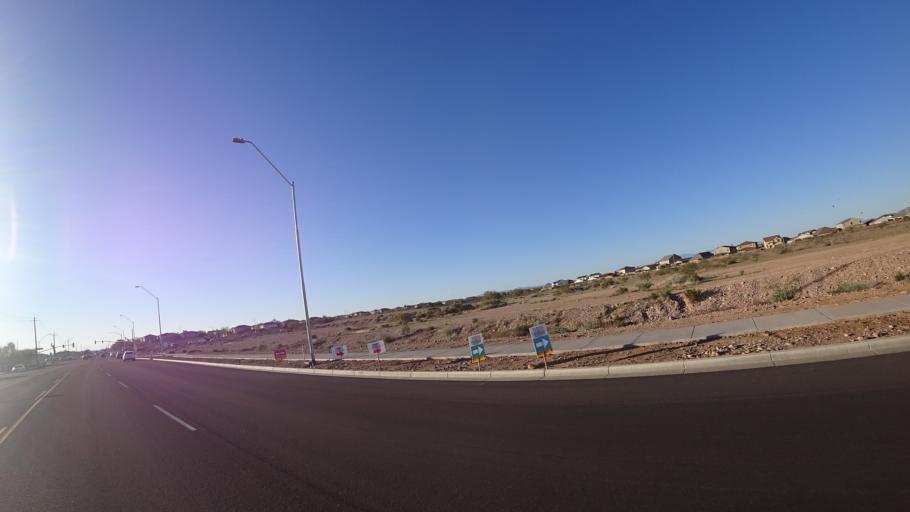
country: US
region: Arizona
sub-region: Maricopa County
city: Sun City West
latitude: 33.6818
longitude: -112.2772
